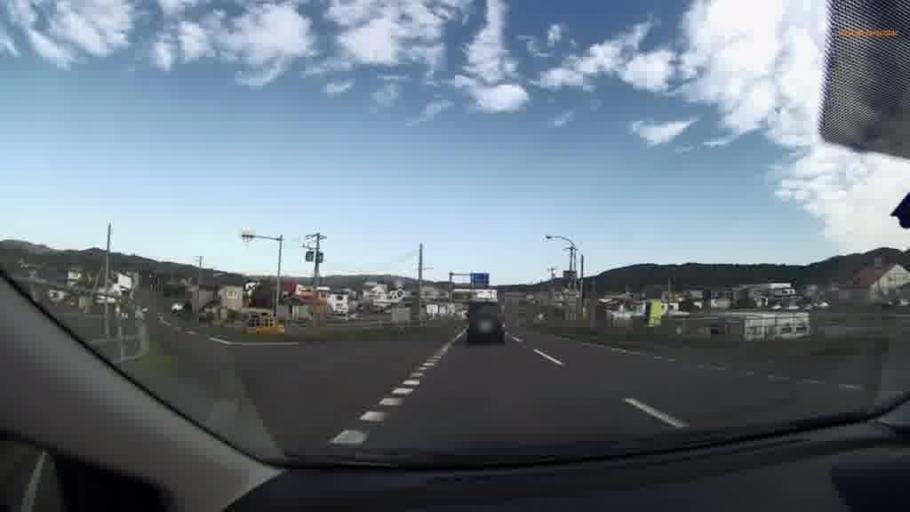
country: JP
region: Hokkaido
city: Kushiro
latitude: 42.9569
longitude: 144.0735
